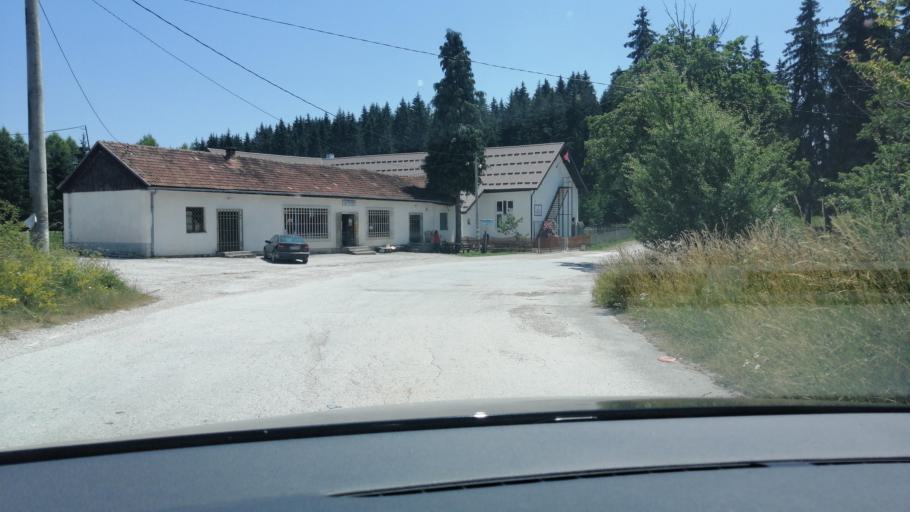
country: RS
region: Central Serbia
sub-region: Zlatiborski Okrug
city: Nova Varos
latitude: 43.4234
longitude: 19.8807
